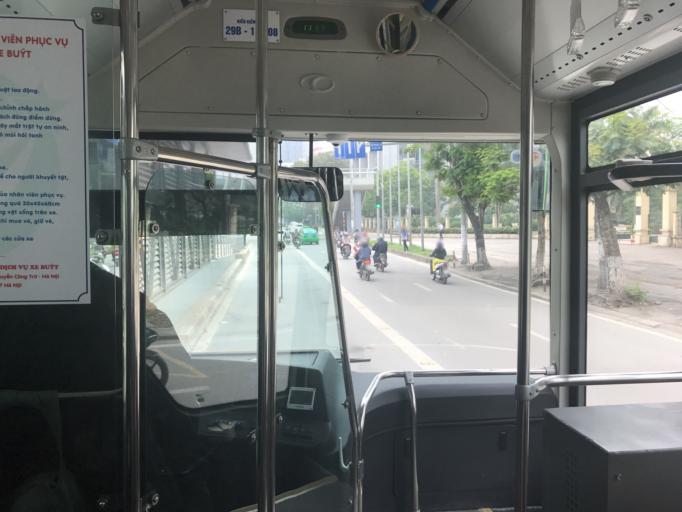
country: VN
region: Ha Noi
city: Dong Da
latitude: 21.0183
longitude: 105.8157
